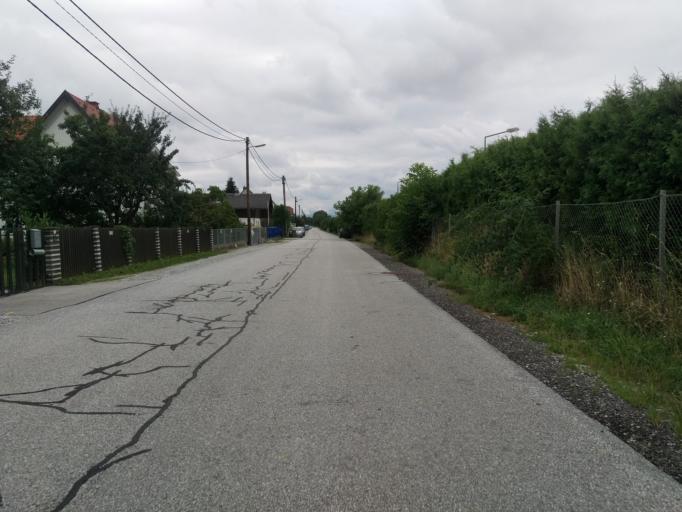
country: AT
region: Styria
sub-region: Politischer Bezirk Graz-Umgebung
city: Raaba
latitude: 47.0391
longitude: 15.4858
